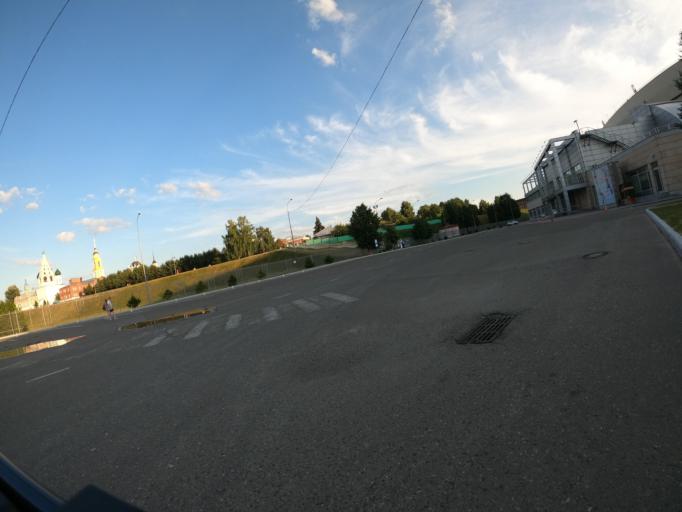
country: RU
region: Moskovskaya
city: Kolomna
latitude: 55.1069
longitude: 38.7538
